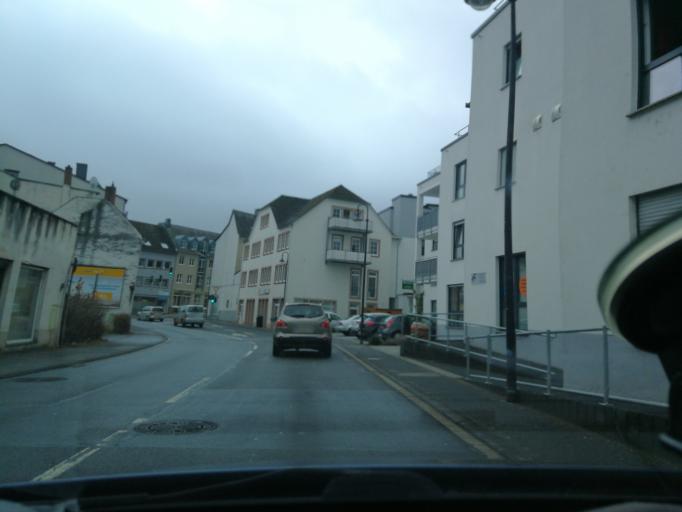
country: DE
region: Rheinland-Pfalz
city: Wittlich
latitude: 49.9847
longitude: 6.8861
